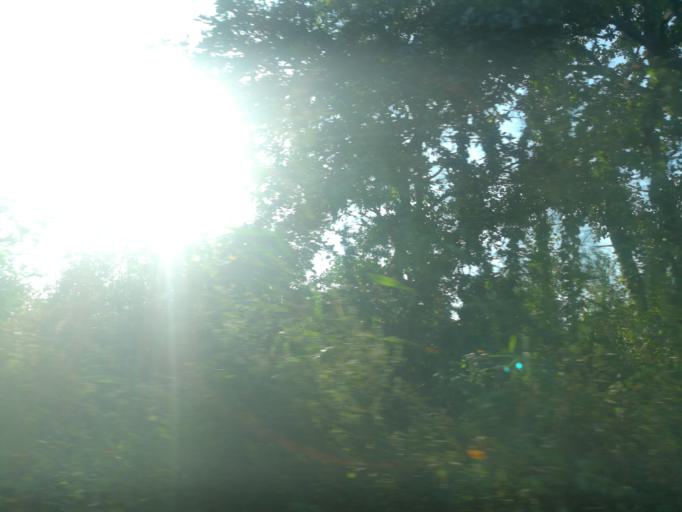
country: NG
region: Ogun
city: Abeokuta
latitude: 7.2356
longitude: 3.3007
